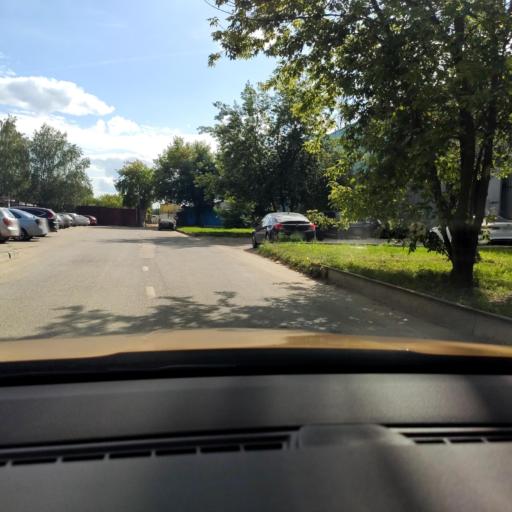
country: RU
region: Moscow
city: Tsaritsyno
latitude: 55.6223
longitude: 37.6359
